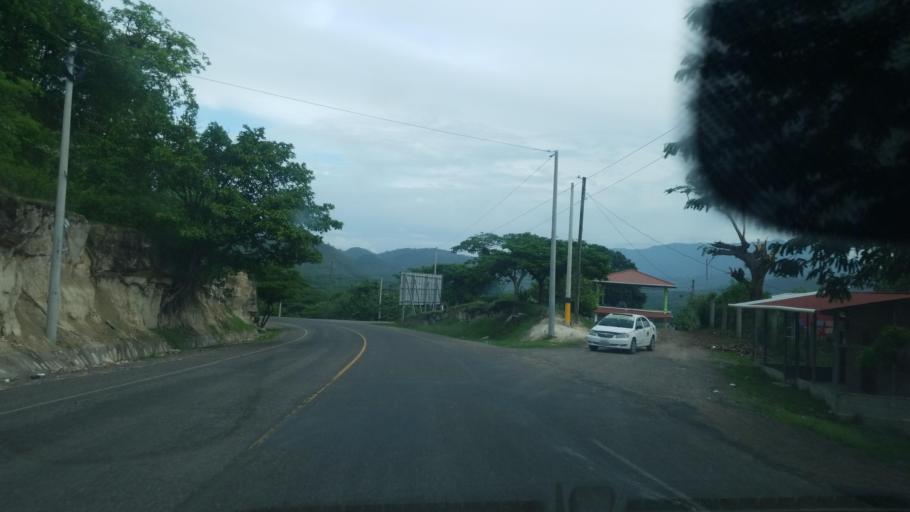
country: HN
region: Santa Barbara
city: Santa Barbara
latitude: 14.8955
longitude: -88.2520
